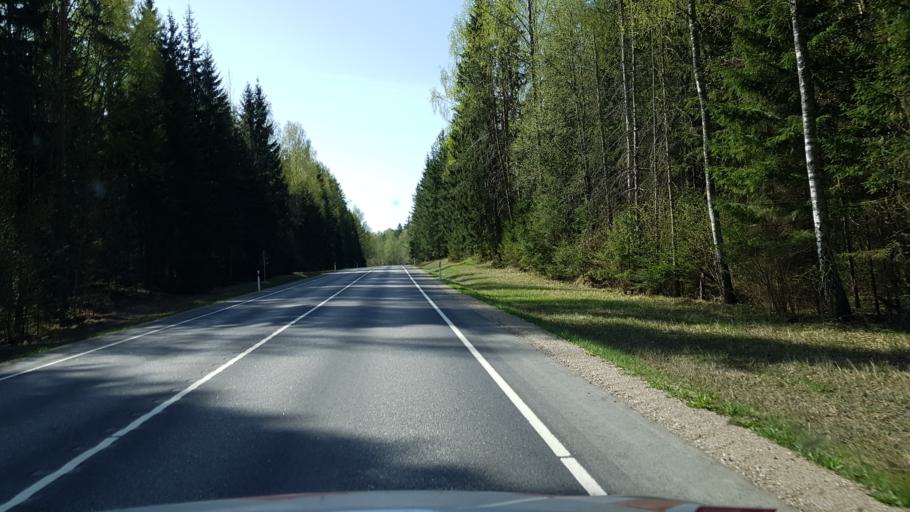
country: EE
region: Viljandimaa
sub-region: Karksi vald
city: Karksi-Nuia
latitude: 58.0707
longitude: 25.6209
